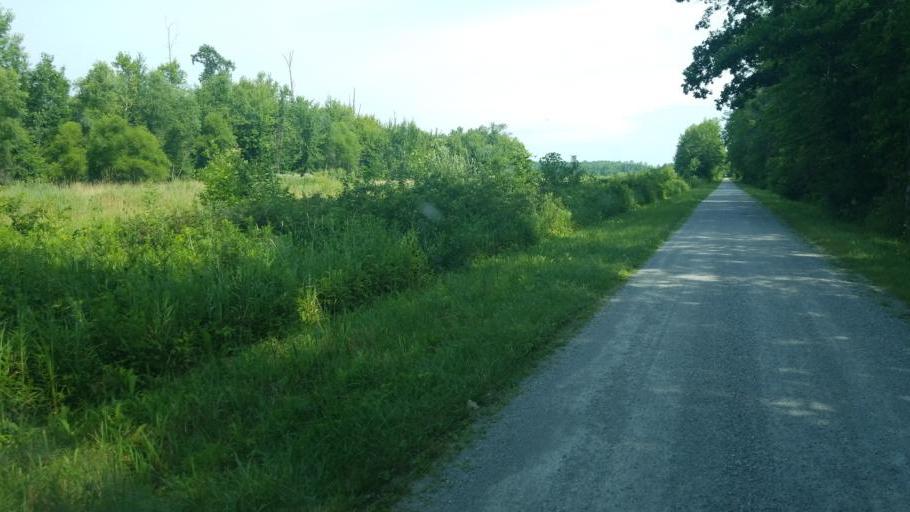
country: US
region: Ohio
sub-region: Wyandot County
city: Upper Sandusky
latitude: 40.7026
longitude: -83.3429
